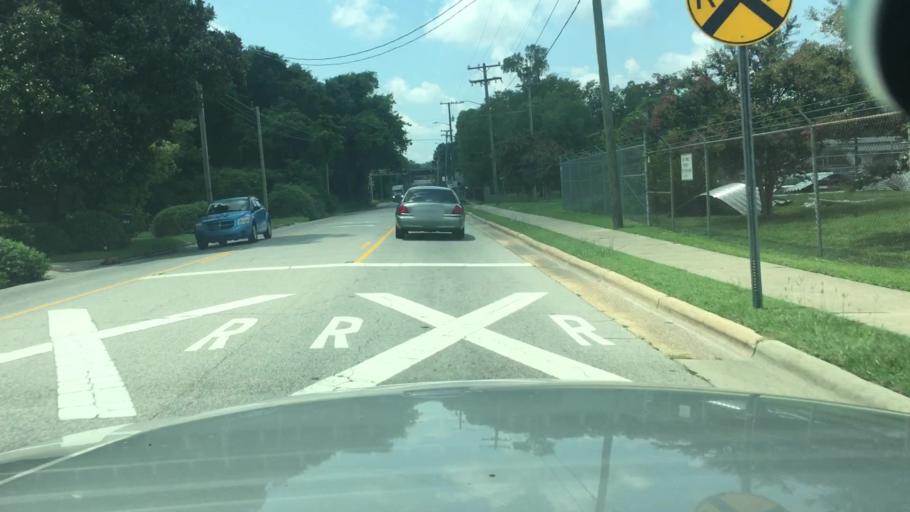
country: US
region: North Carolina
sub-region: Cumberland County
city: Fayetteville
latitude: 35.0410
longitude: -78.8837
